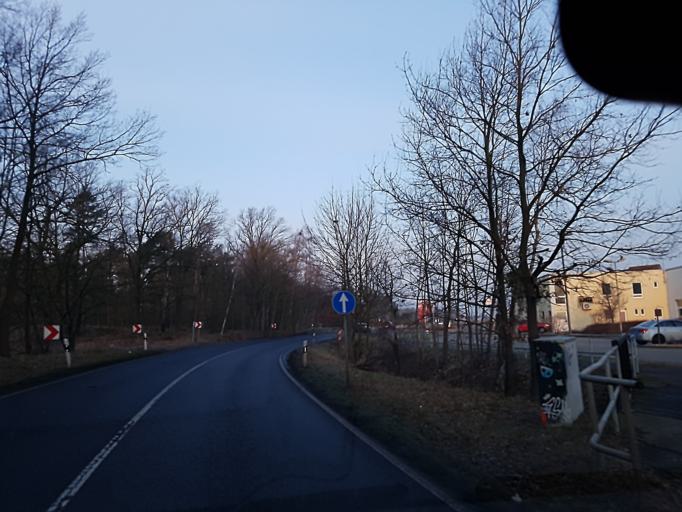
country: DE
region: Saxony-Anhalt
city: Abtsdorf
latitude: 51.8597
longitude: 12.7204
